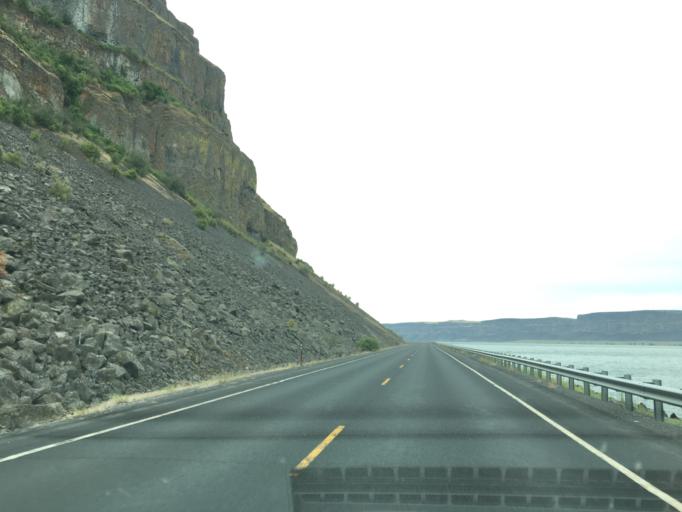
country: US
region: Washington
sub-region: Okanogan County
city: Coulee Dam
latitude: 47.8223
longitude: -119.1430
